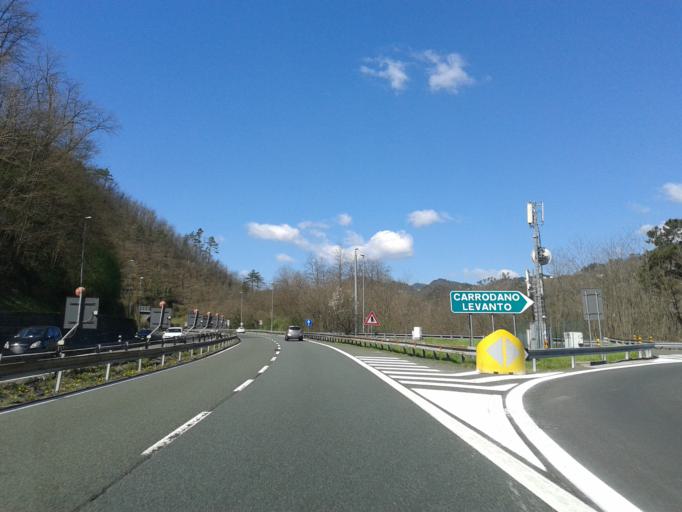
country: IT
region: Liguria
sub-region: Provincia di La Spezia
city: Carrodano
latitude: 44.2361
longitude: 9.6509
